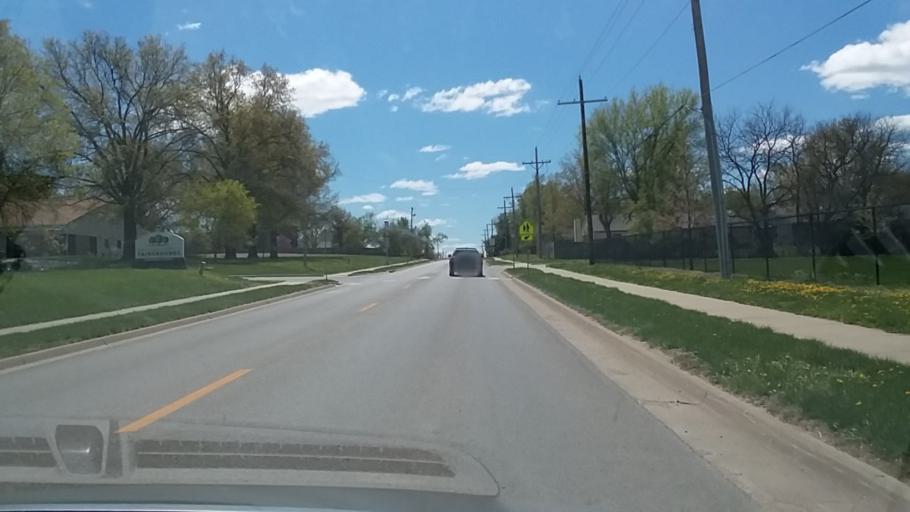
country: US
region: Kansas
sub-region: Douglas County
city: Lawrence
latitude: 38.9471
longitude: -95.2142
